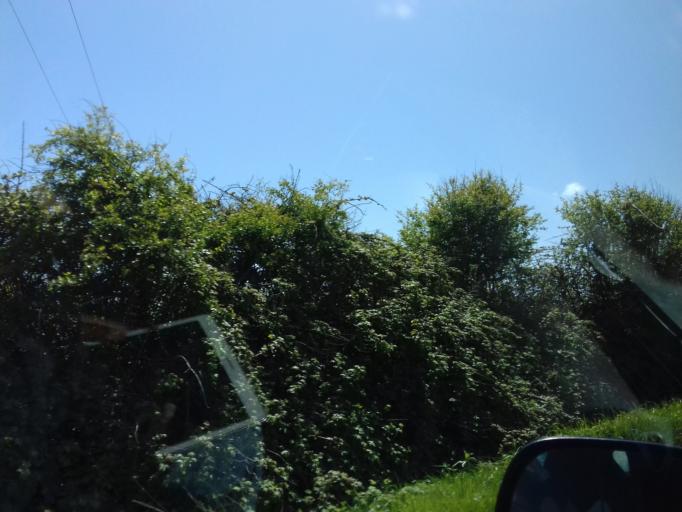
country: IE
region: Munster
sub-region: Waterford
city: Dunmore East
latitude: 52.1690
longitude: -6.8820
